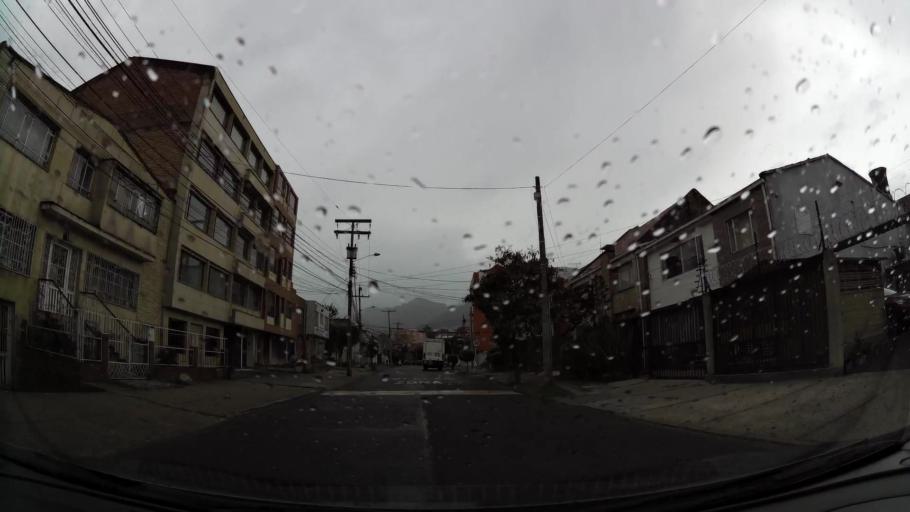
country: CO
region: Bogota D.C.
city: Bogota
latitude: 4.6263
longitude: -74.0784
